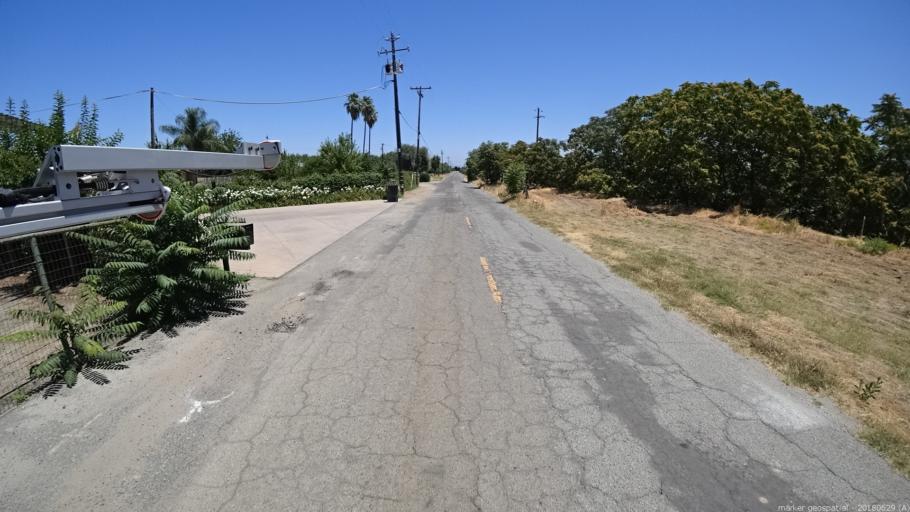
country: US
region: California
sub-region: Madera County
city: Parksdale
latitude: 37.0023
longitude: -119.9984
